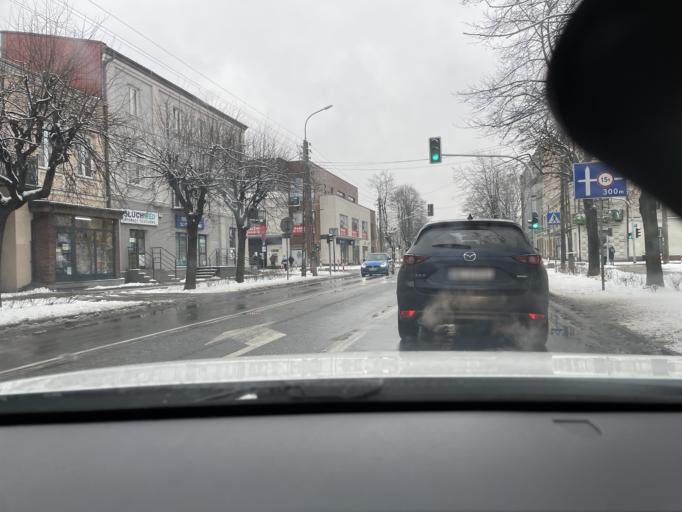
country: PL
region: Masovian Voivodeship
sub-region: Powiat zyrardowski
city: Zyrardow
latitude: 52.0539
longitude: 20.4403
